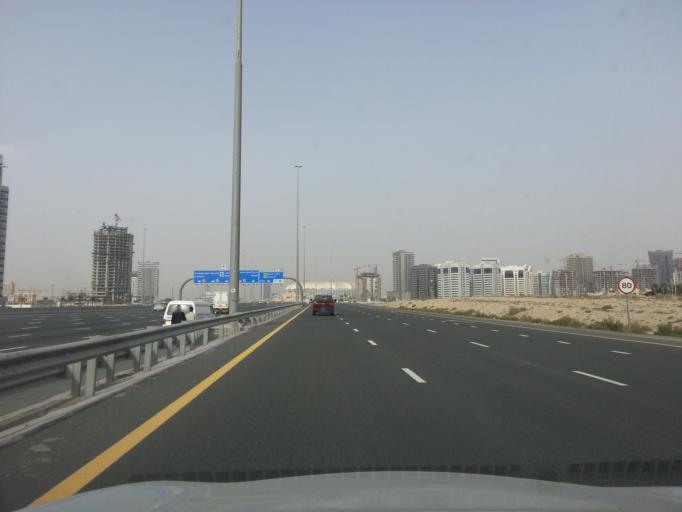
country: AE
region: Dubai
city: Dubai
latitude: 25.0441
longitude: 55.2050
